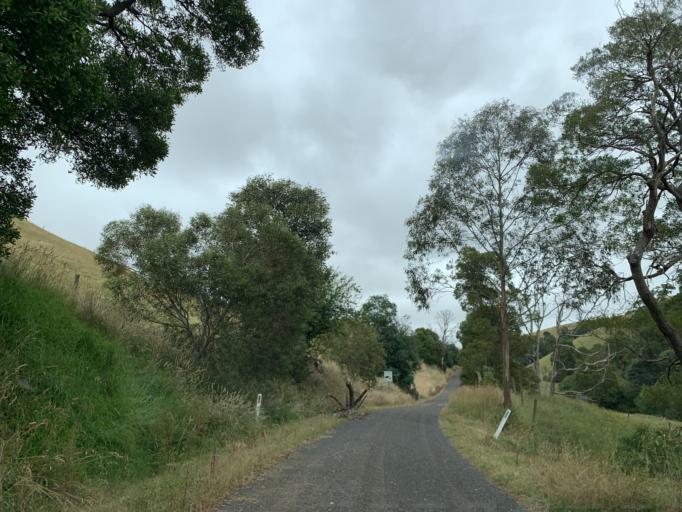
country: AU
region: Victoria
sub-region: Baw Baw
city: Warragul
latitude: -38.3319
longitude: 145.8578
